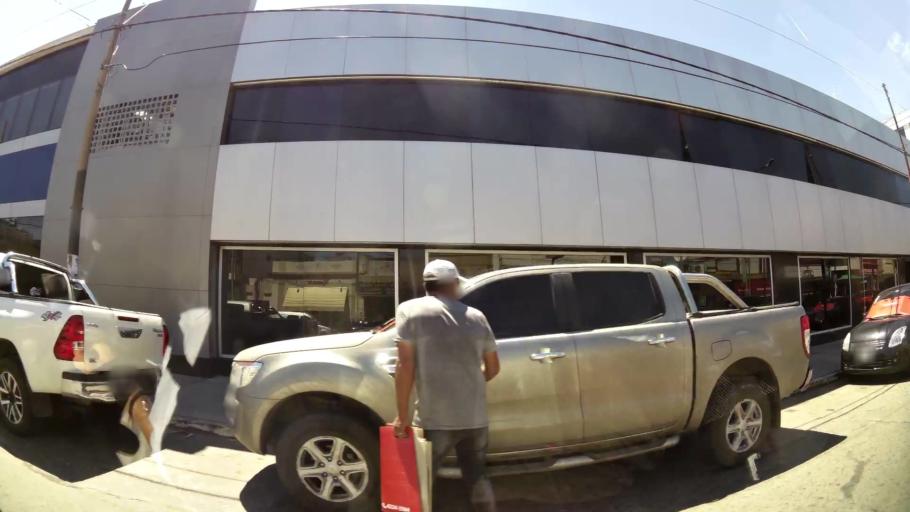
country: AR
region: Buenos Aires
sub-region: Partido de Quilmes
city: Quilmes
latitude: -34.7187
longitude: -58.2741
